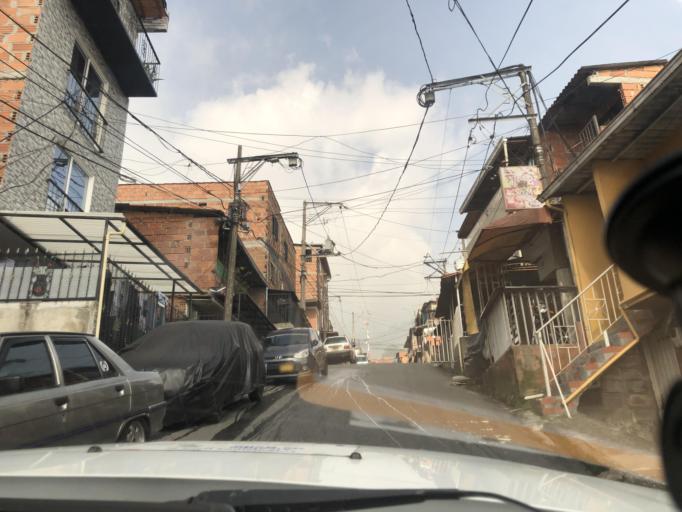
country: CO
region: Antioquia
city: Bello
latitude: 6.3134
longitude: -75.5775
